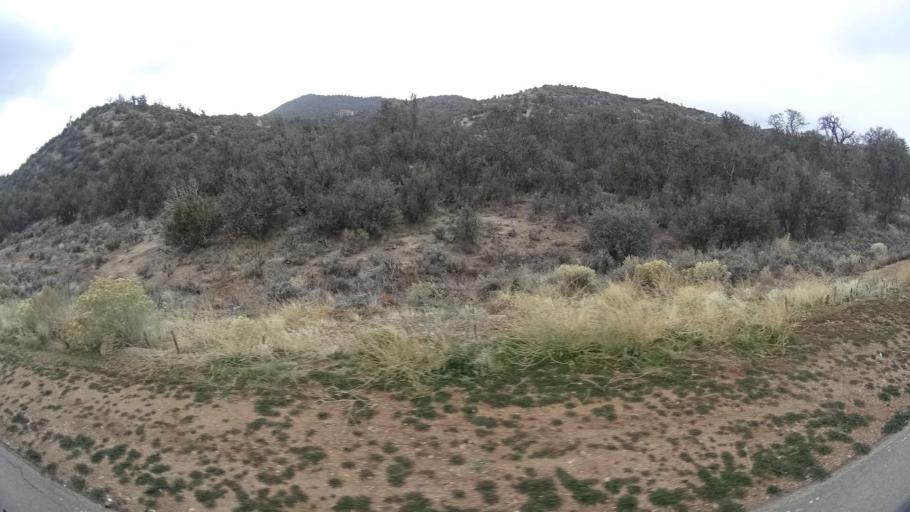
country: US
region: California
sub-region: Kern County
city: Tehachapi
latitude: 35.1740
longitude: -118.3612
